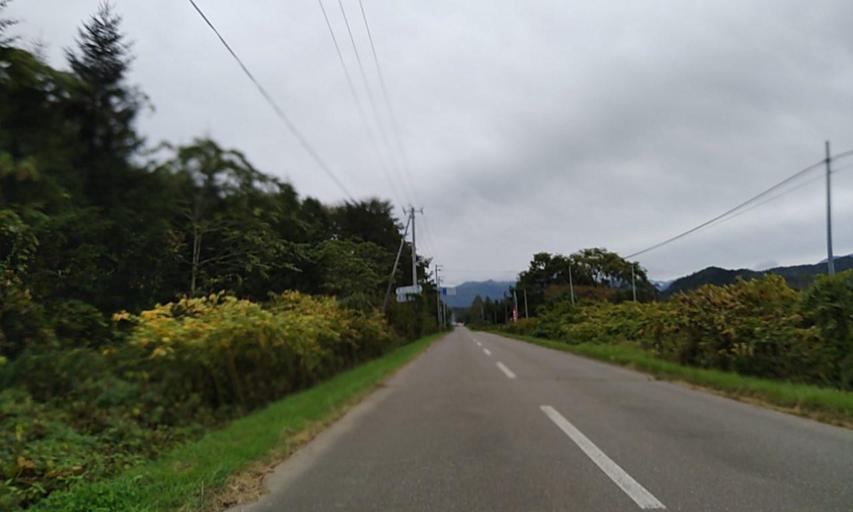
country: JP
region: Hokkaido
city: Obihiro
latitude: 42.6686
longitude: 143.0360
